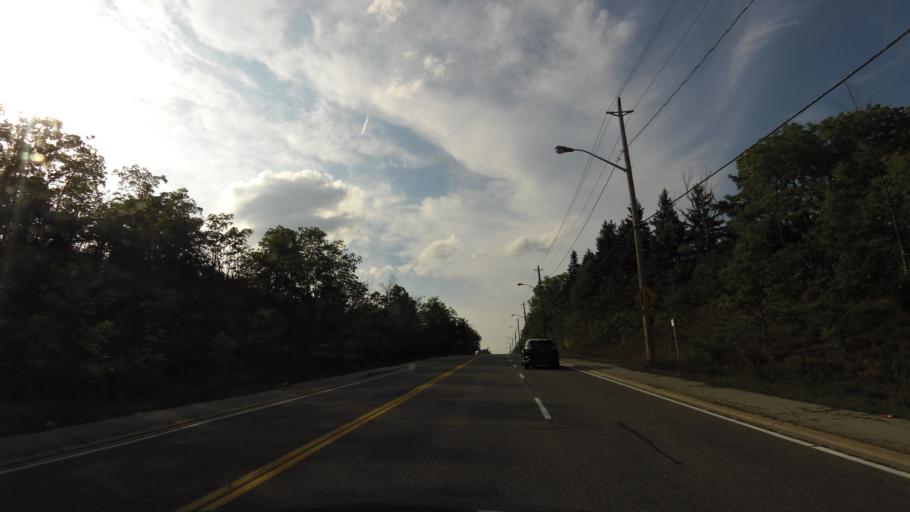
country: CA
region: Ontario
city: Burlington
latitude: 43.3656
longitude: -79.8586
